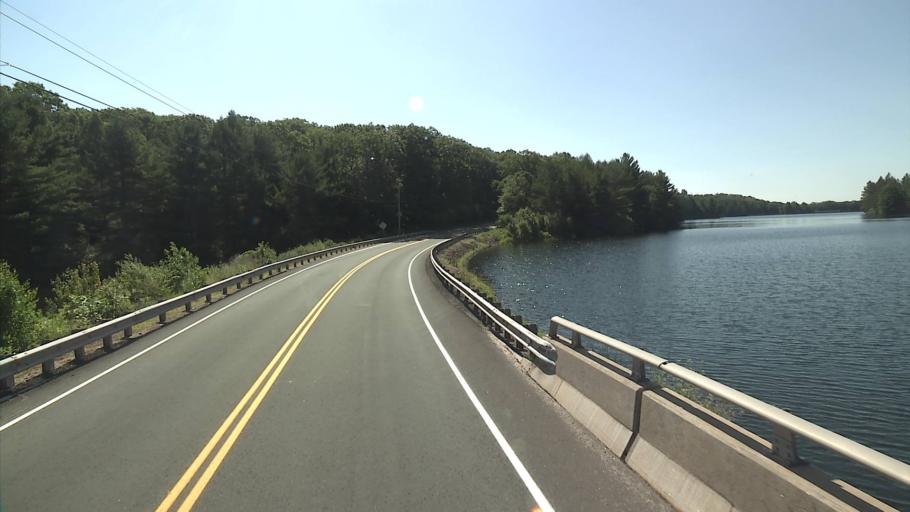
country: US
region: Connecticut
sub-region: Litchfield County
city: Northwest Harwinton
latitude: 41.7486
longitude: -73.0216
